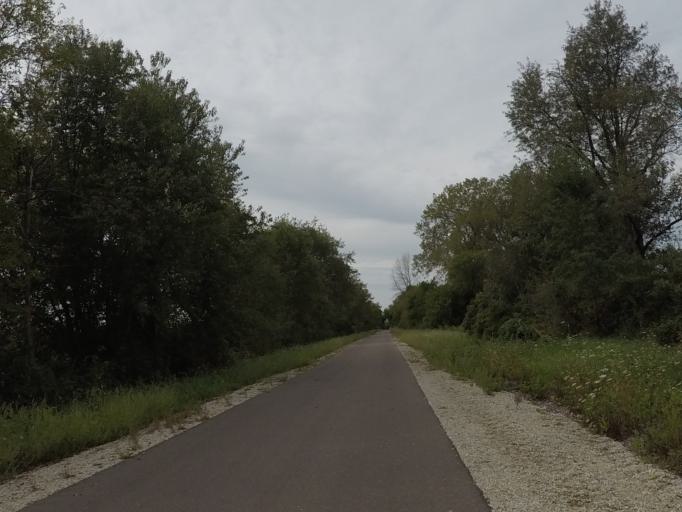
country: US
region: Wisconsin
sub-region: Sauk County
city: Prairie du Sac
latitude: 43.3415
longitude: -89.7439
